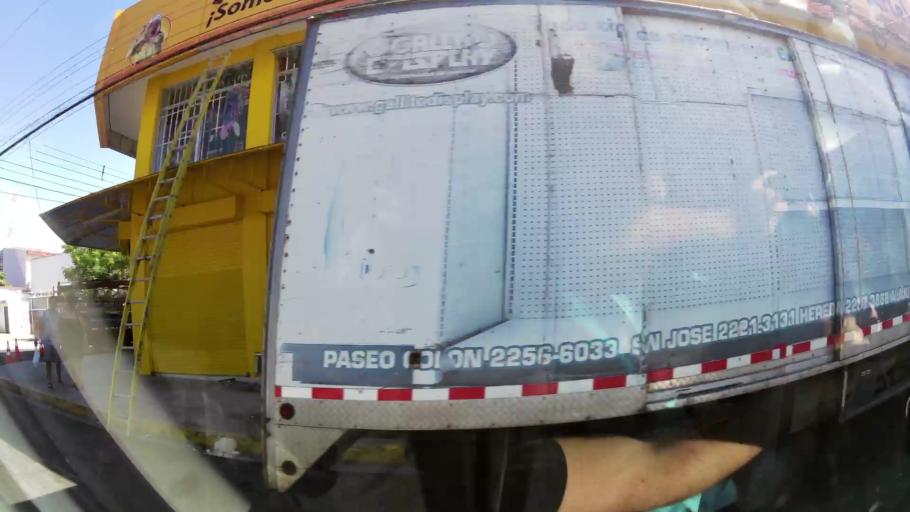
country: CR
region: Guanacaste
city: Liberia
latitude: 10.6294
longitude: -85.4398
